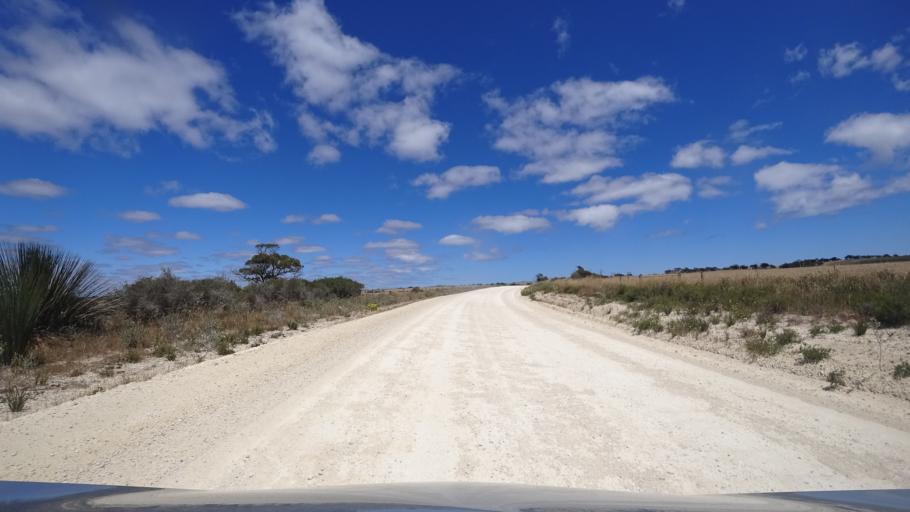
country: AU
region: South Australia
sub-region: Kangaroo Island
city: Kingscote
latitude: -35.6482
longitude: 137.3649
